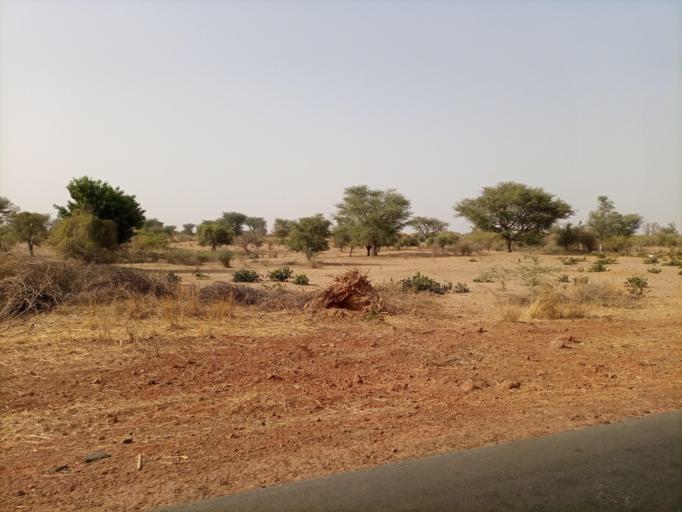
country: SN
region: Fatick
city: Foundiougne
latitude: 14.1242
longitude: -16.4244
